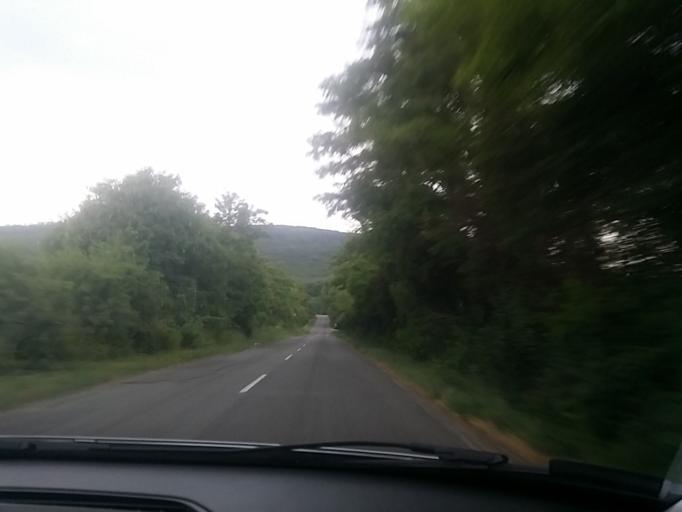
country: HU
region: Nograd
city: Paszto
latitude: 47.9328
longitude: 19.6151
